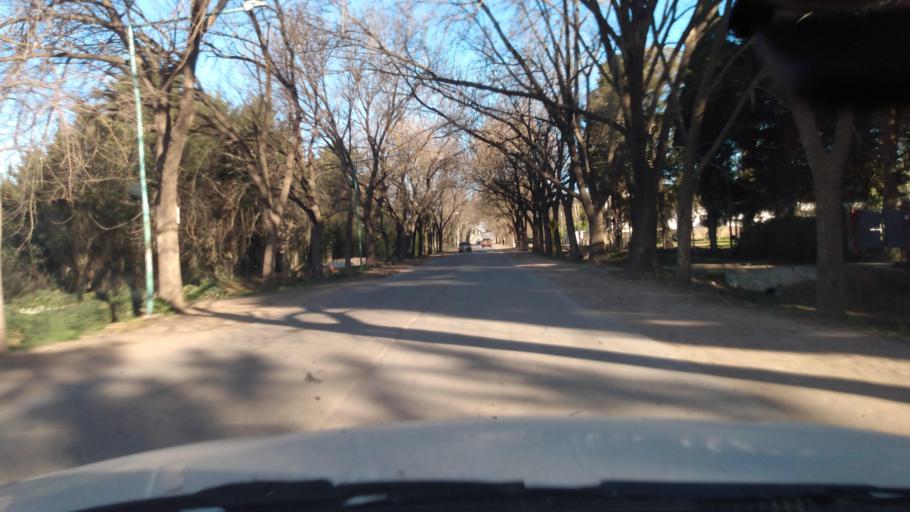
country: AR
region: Buenos Aires
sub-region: Partido de Lujan
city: Lujan
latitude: -34.6275
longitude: -59.2523
